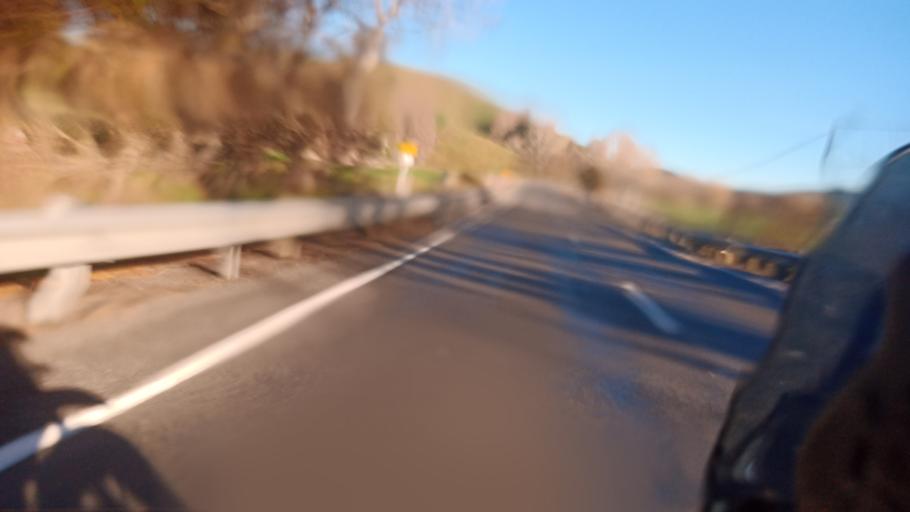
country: NZ
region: Hawke's Bay
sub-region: Wairoa District
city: Wairoa
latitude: -39.0167
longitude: 177.3636
